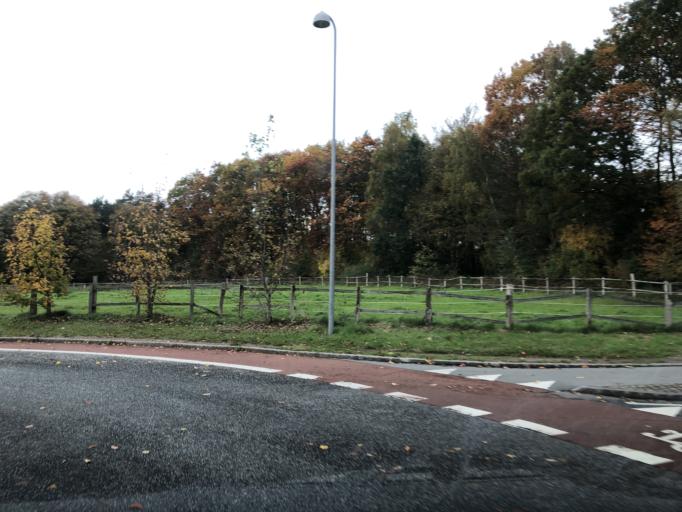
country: DK
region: Capital Region
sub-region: Lyngby-Tarbaek Kommune
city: Kongens Lyngby
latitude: 55.8027
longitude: 12.4998
